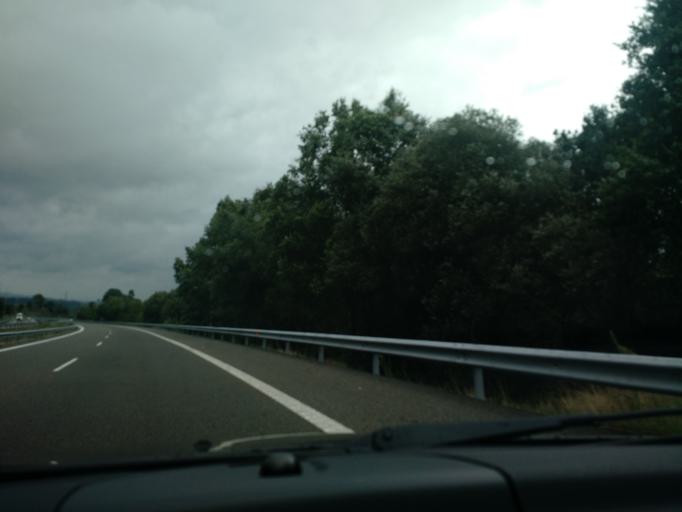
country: ES
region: Galicia
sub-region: Provincia da Coruna
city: Oroso
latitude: 42.9551
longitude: -8.4563
